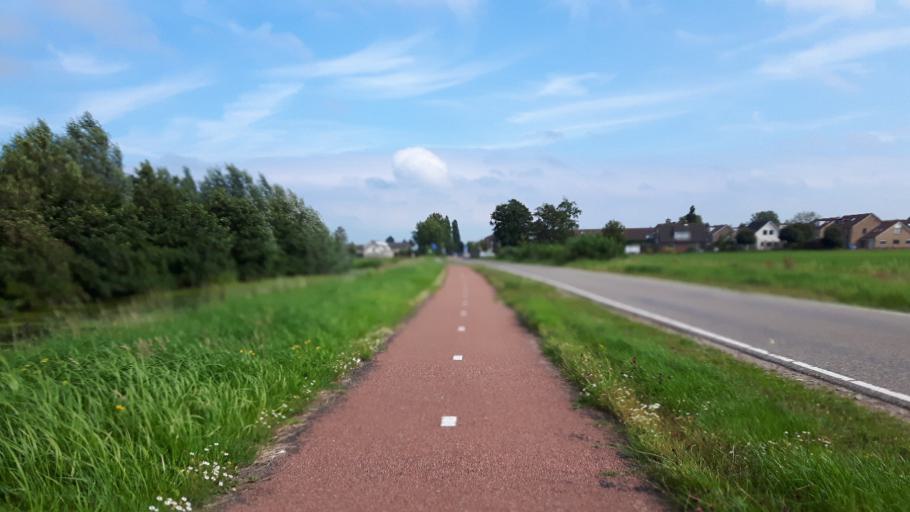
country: NL
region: South Holland
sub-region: Gemeente Nieuwkoop
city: Nieuwkoop
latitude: 52.1192
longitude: 4.8296
